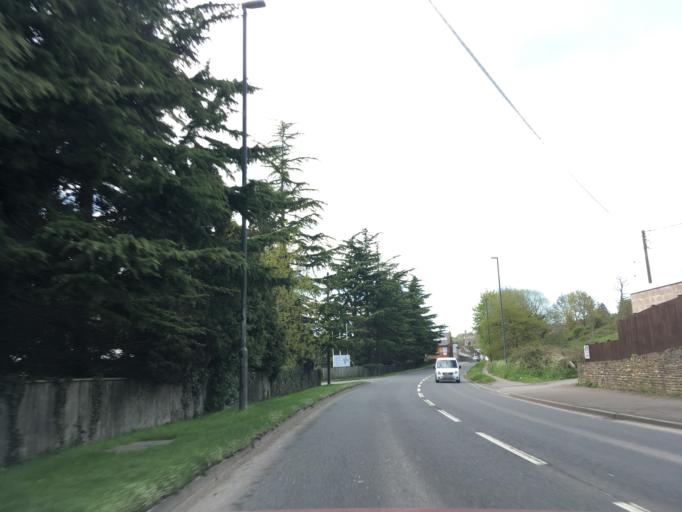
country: GB
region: England
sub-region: Gloucestershire
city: Brimscombe
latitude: 51.7283
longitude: -2.2030
